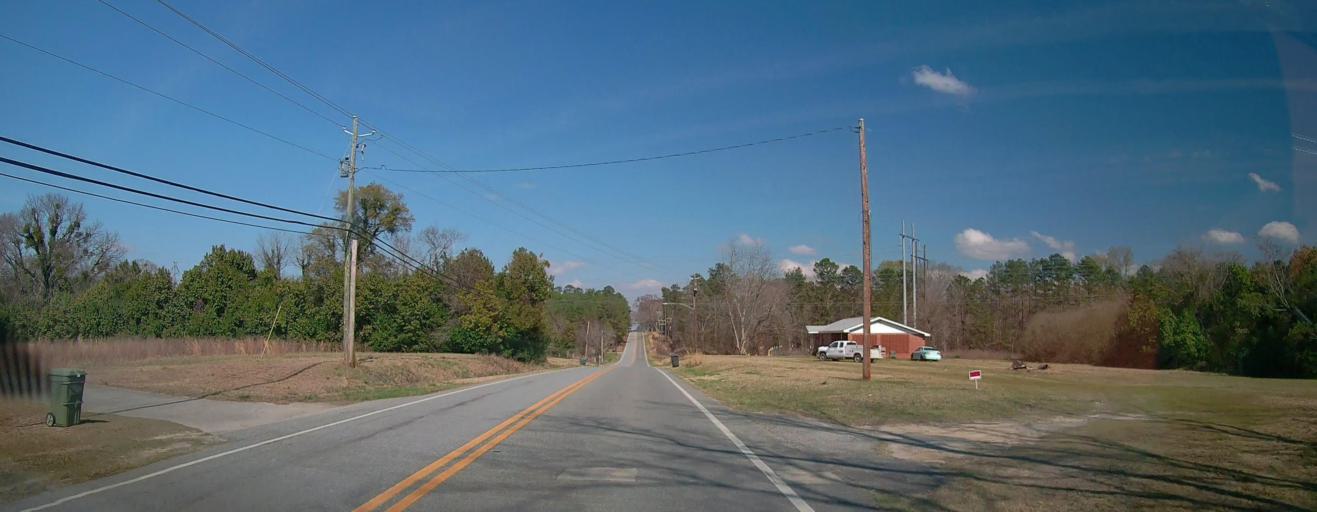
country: US
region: Georgia
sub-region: Wilkinson County
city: Gordon
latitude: 32.8880
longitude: -83.3181
